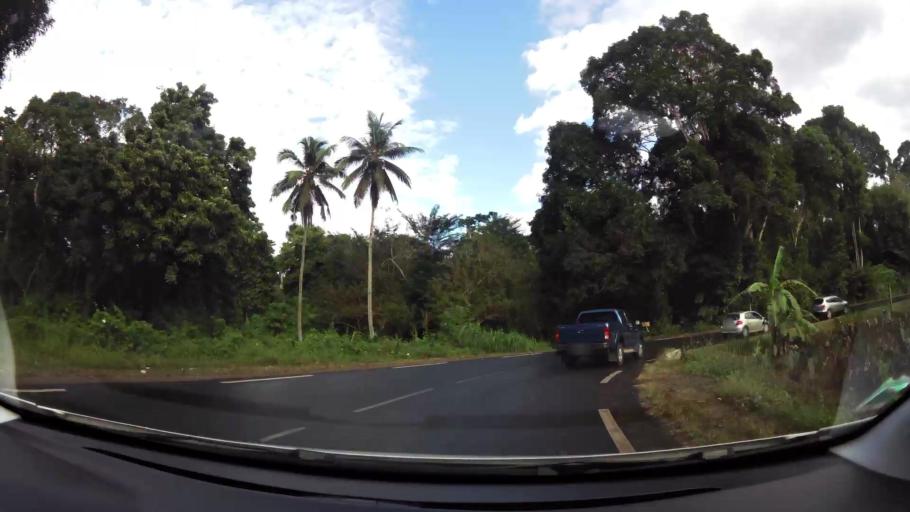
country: YT
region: Ouangani
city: Ouangani
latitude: -12.8367
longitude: 45.1433
